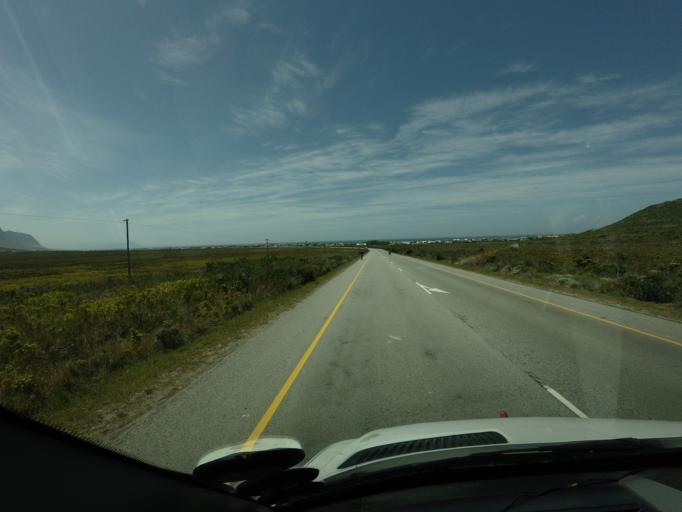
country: ZA
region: Western Cape
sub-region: Overberg District Municipality
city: Grabouw
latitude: -34.3575
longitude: 18.8622
